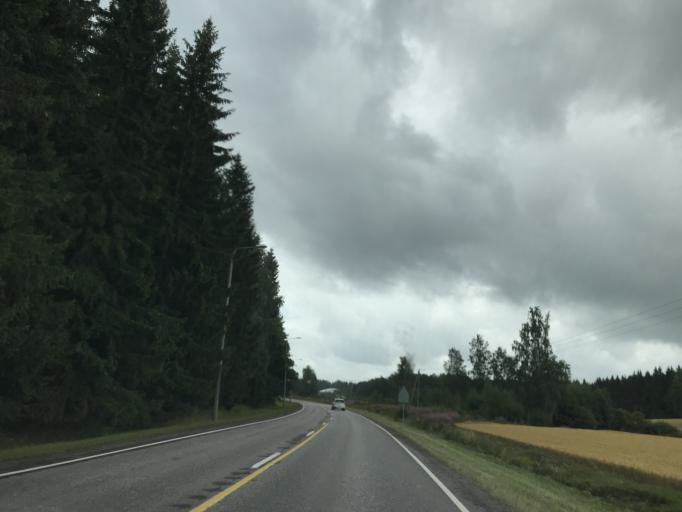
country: FI
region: Uusimaa
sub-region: Raaseporin
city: Ekenaes
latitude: 60.0017
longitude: 23.4026
